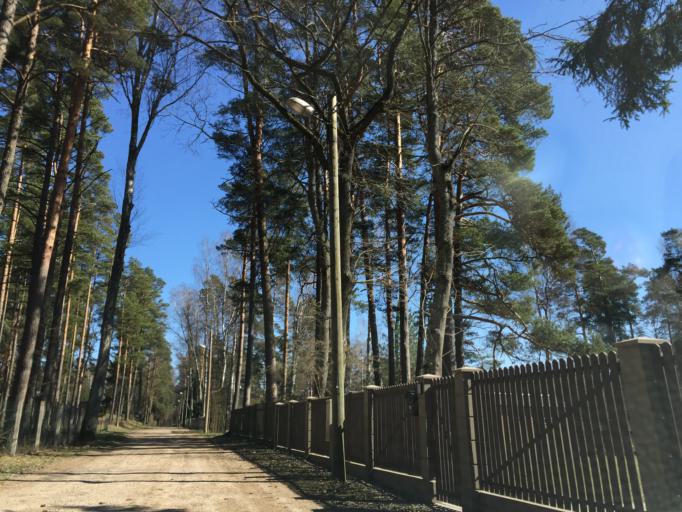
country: LV
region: Jurmala
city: Jurmala
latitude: 56.9459
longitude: 23.6989
